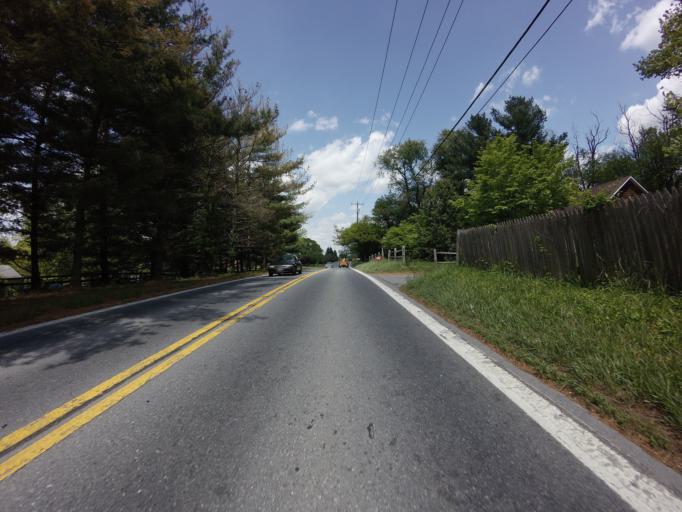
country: US
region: Maryland
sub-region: Frederick County
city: Green Valley
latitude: 39.3242
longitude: -77.2806
